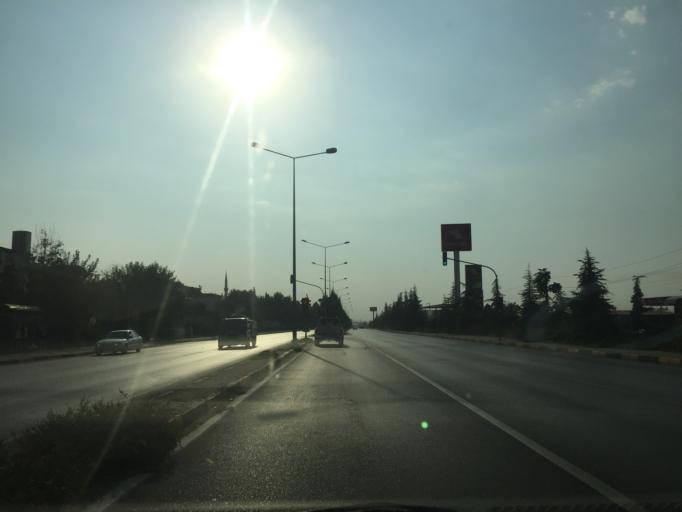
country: TR
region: Manisa
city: Salihli
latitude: 38.4895
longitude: 28.1521
